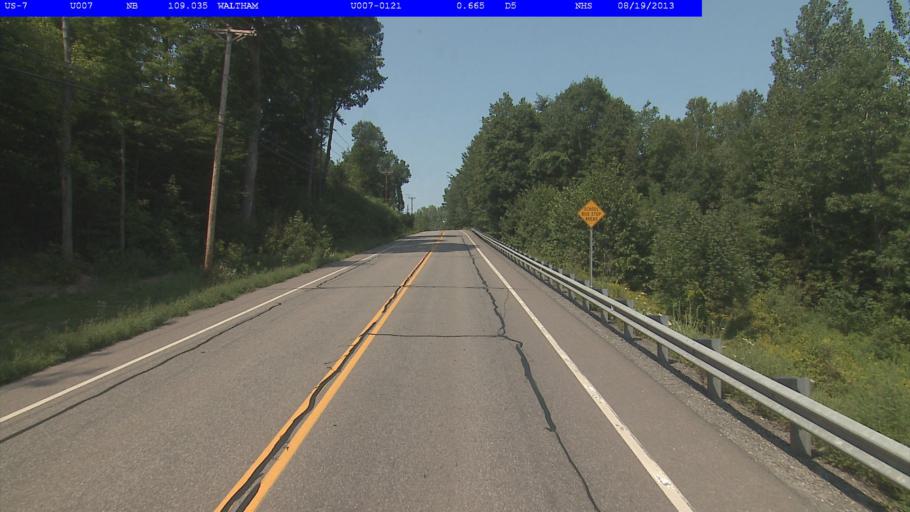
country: US
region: Vermont
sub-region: Addison County
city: Vergennes
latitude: 44.1548
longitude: -73.2191
